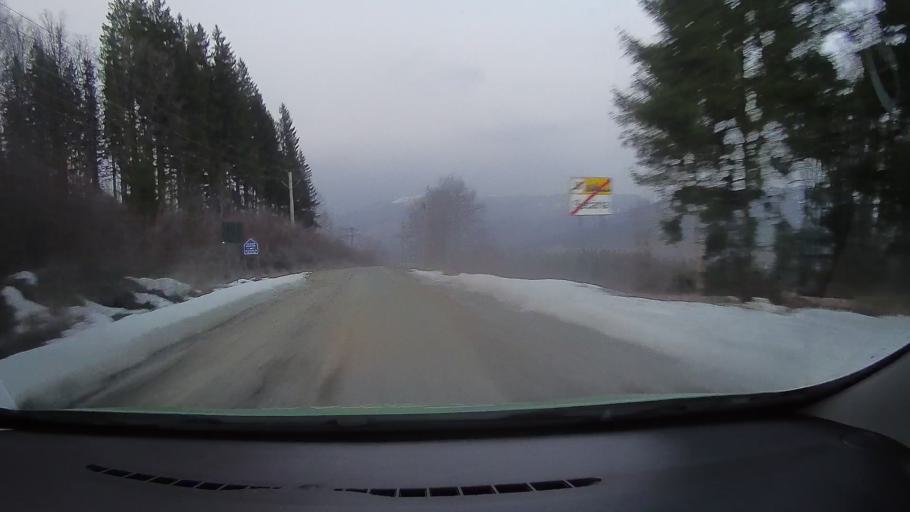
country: RO
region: Prahova
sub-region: Comuna Valea Doftanei
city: Tesila
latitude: 45.2910
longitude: 25.7047
